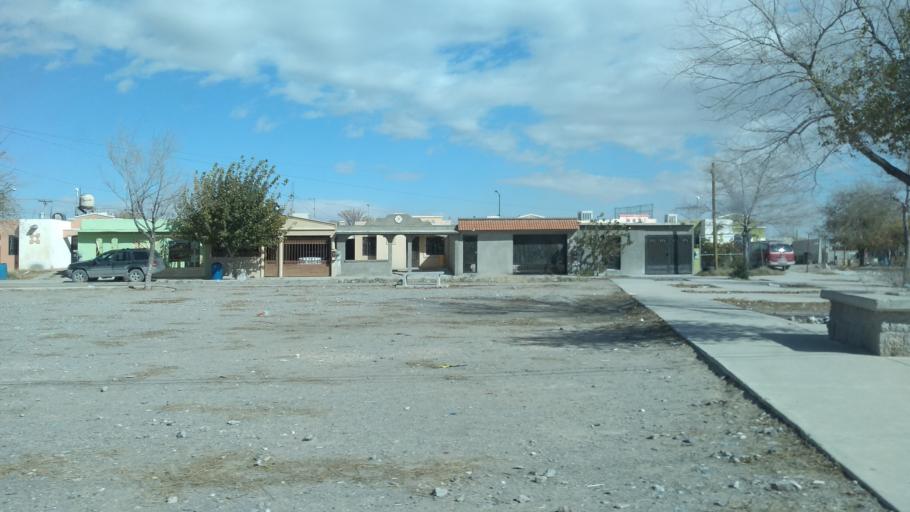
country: US
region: Texas
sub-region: El Paso County
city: Socorro Mission Number 1 Colonia
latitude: 31.5855
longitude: -106.3545
